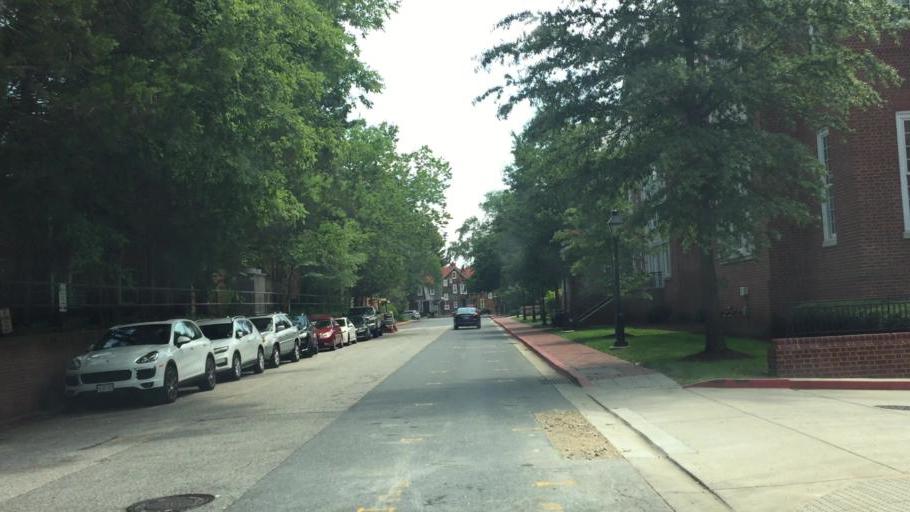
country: US
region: Maryland
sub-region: Anne Arundel County
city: Annapolis
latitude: 38.9811
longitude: -76.4926
